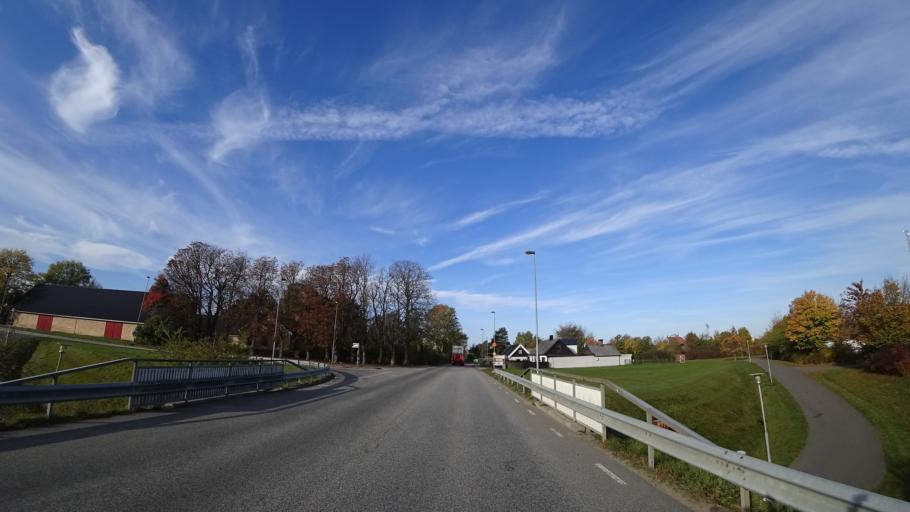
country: SE
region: Skane
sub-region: Staffanstorps Kommun
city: Staffanstorp
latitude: 55.6373
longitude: 13.2186
